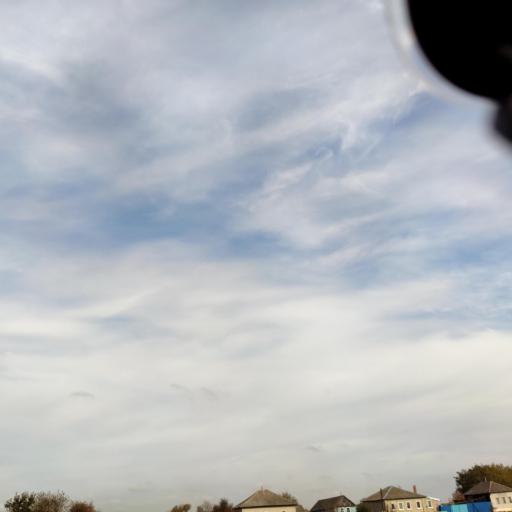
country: RU
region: Voronezj
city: Rossosh'
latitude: 51.1960
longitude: 38.7768
